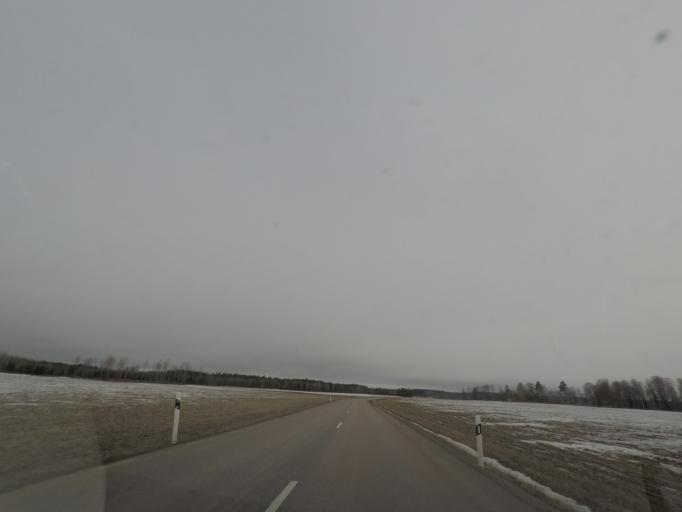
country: SE
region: Vaestmanland
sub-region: Vasteras
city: Skultuna
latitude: 59.7341
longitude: 16.4137
